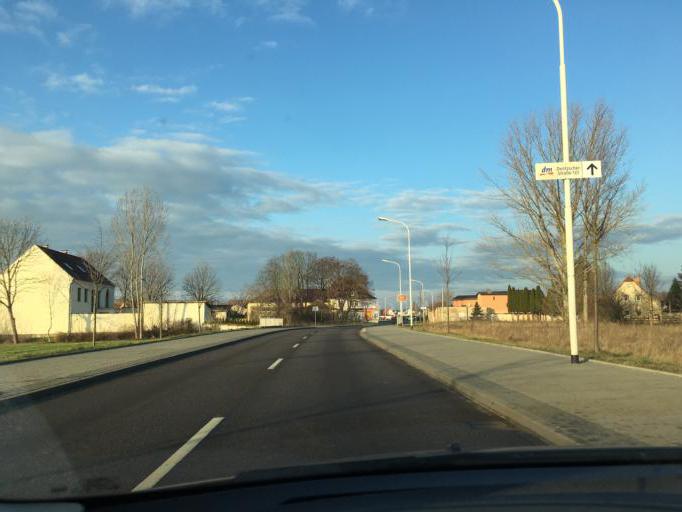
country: DE
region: Saxony-Anhalt
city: Dolbau
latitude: 51.4782
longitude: 12.0390
